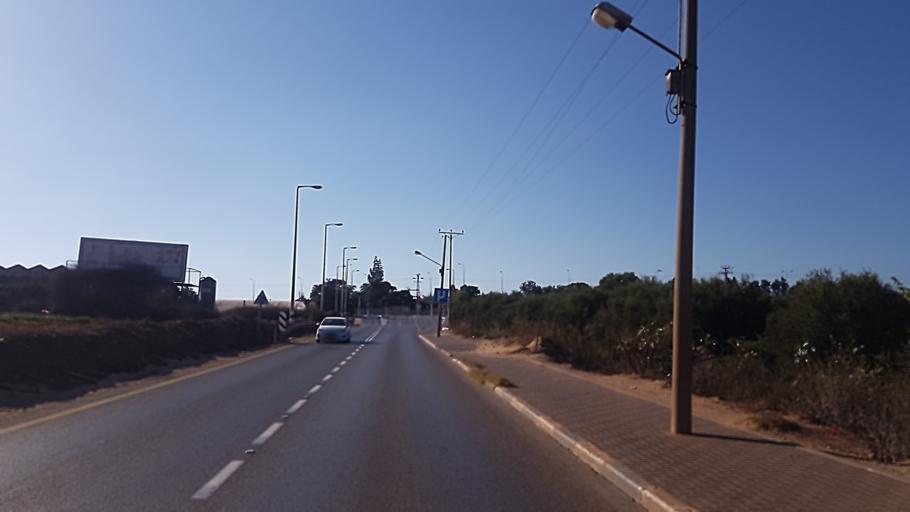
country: IL
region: Central District
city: Kfar Saba
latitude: 32.1987
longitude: 34.9182
